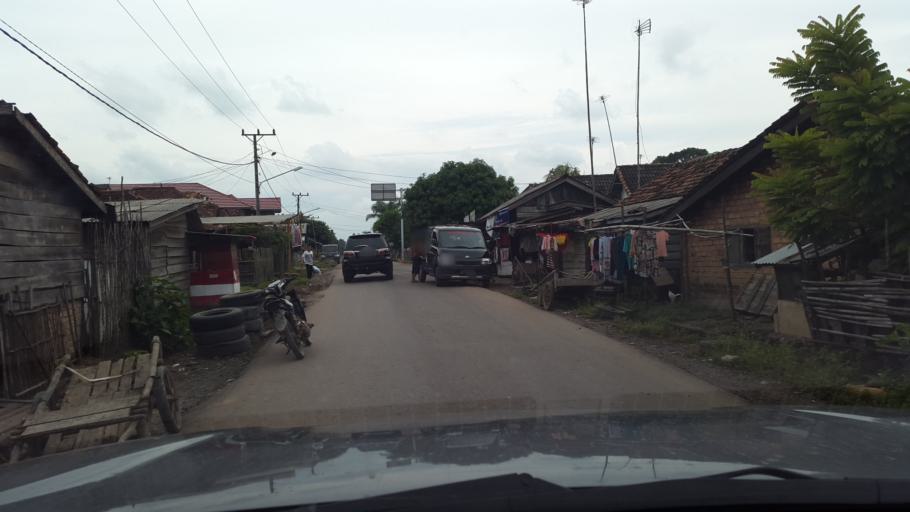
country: ID
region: South Sumatra
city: Gunungmenang
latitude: -3.3158
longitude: 104.0204
